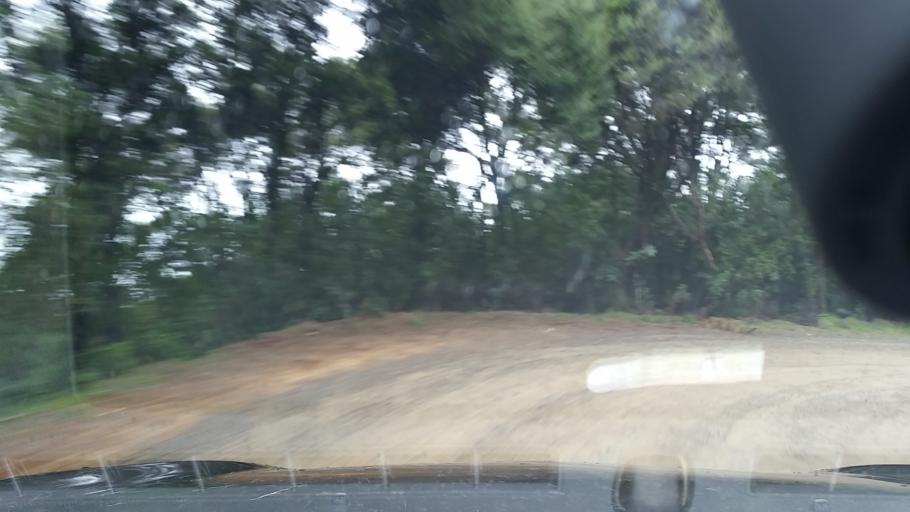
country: NZ
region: Marlborough
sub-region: Marlborough District
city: Picton
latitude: -41.3694
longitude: 174.0664
